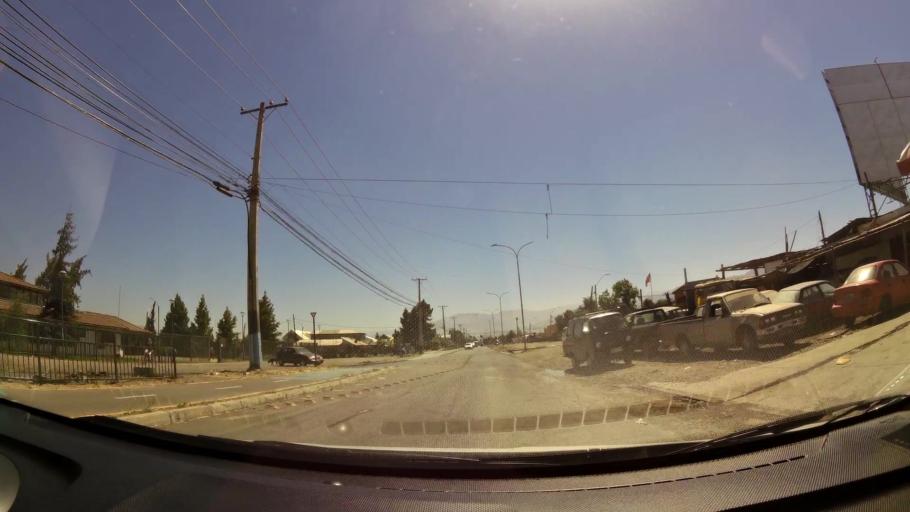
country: CL
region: O'Higgins
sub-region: Provincia de Cachapoal
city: Rancagua
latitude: -34.1672
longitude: -70.7168
